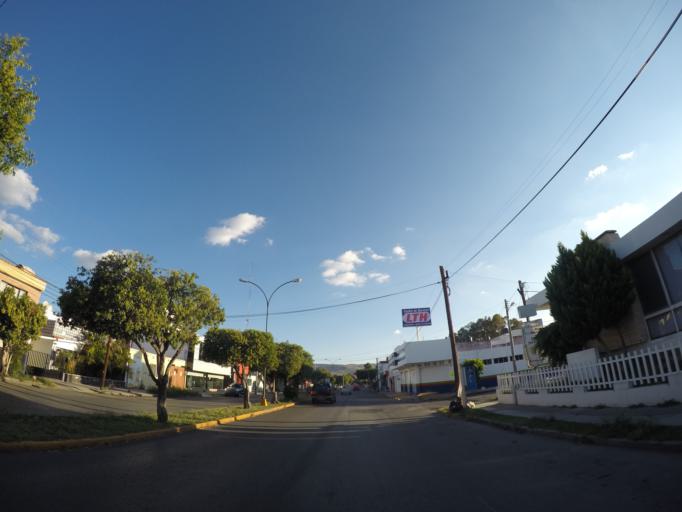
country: MX
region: San Luis Potosi
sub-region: San Luis Potosi
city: San Luis Potosi
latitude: 22.1439
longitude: -100.9854
